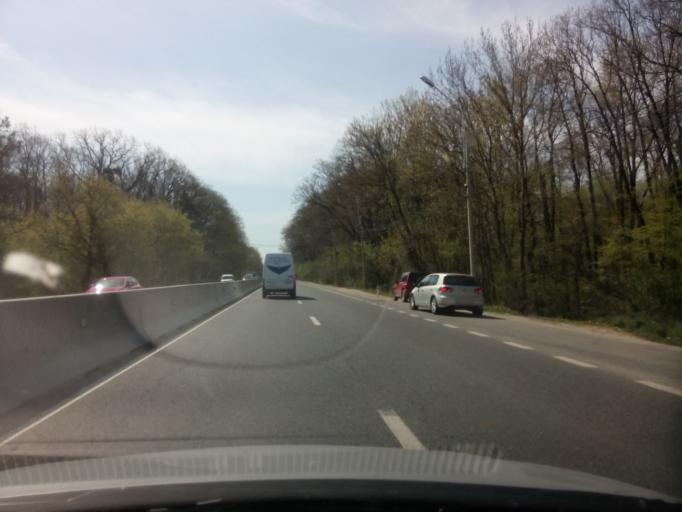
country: RO
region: Ilfov
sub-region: Comuna Corbeanca
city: Corbeanca
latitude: 44.5896
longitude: 26.0708
